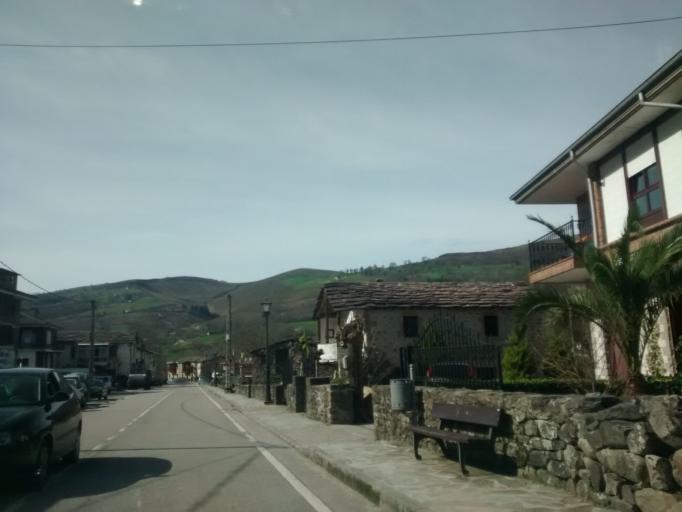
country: ES
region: Cantabria
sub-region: Provincia de Cantabria
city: Vega de Pas
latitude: 43.1549
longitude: -3.7820
